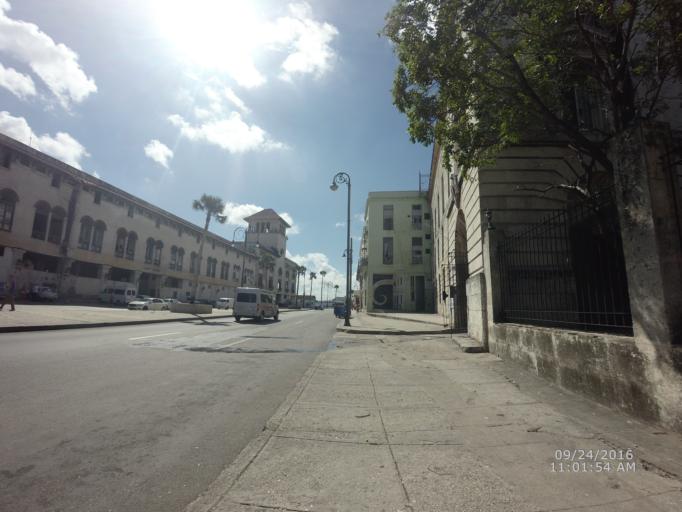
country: CU
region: La Habana
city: La Habana Vieja
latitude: 23.1362
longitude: -82.3478
